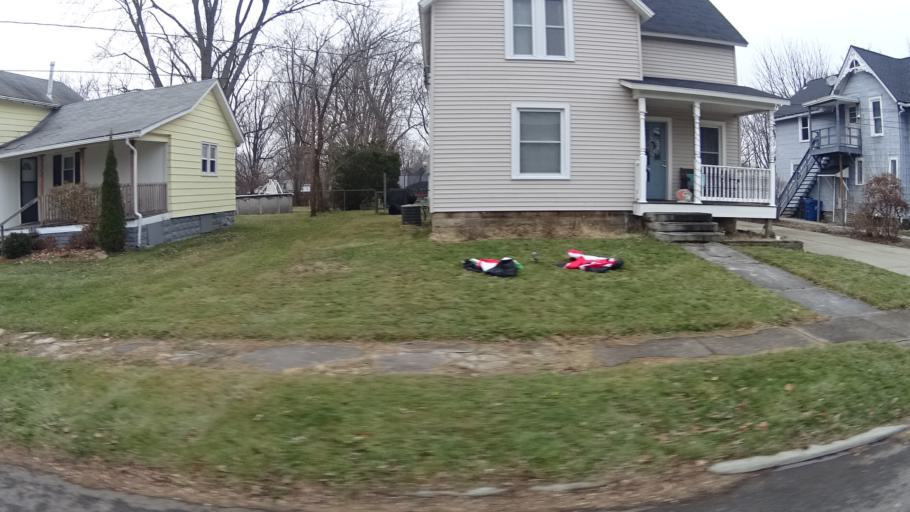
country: US
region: Ohio
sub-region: Lorain County
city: Amherst
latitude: 41.3937
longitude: -82.2191
